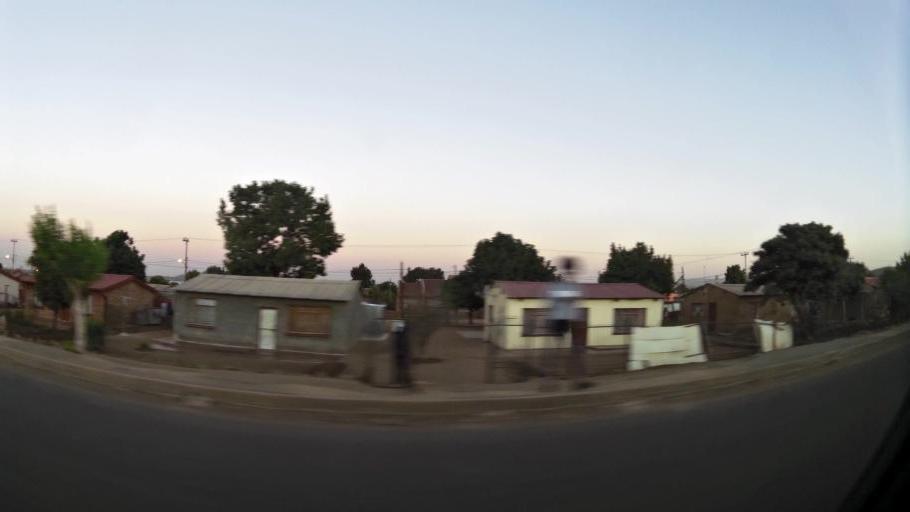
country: ZA
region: North-West
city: Ga-Rankuwa
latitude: -25.5902
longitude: 27.9841
